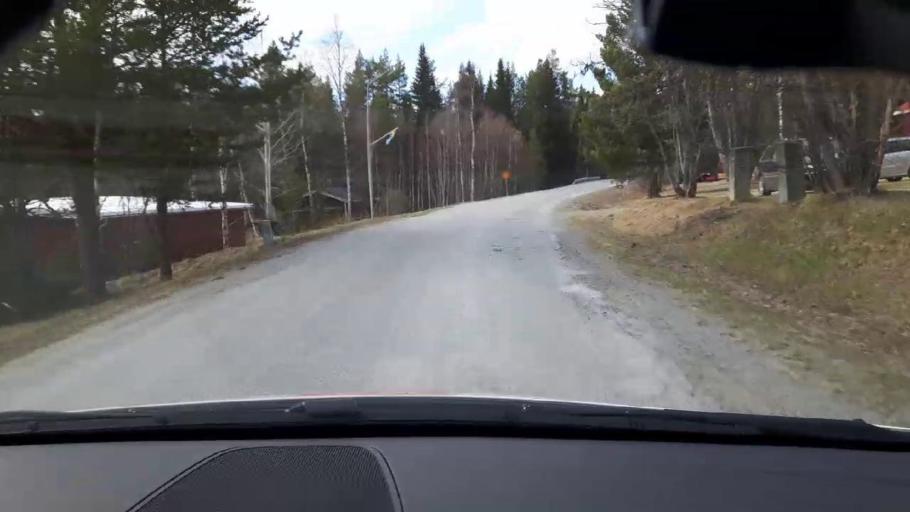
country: SE
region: Jaemtland
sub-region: Bergs Kommun
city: Hoverberg
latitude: 62.6674
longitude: 14.7470
